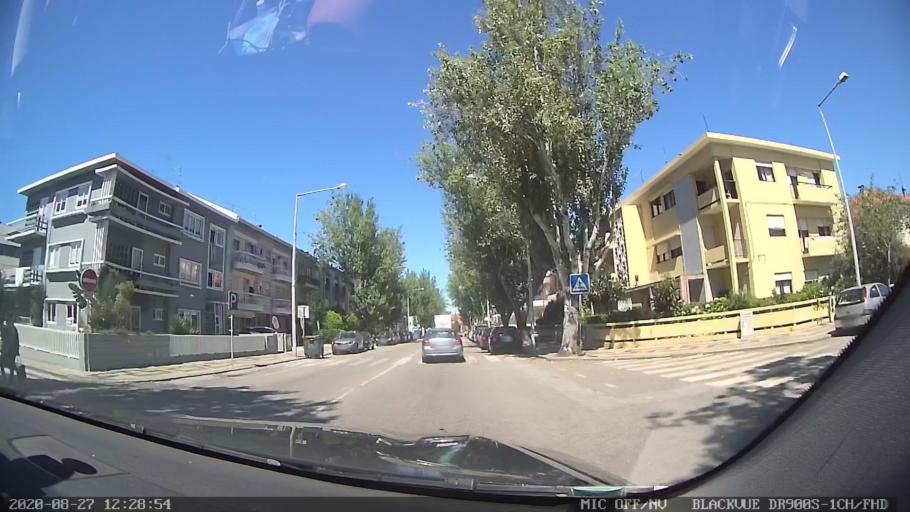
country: PT
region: Aveiro
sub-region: Aveiro
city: Aveiro
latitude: 40.6380
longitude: -8.6492
